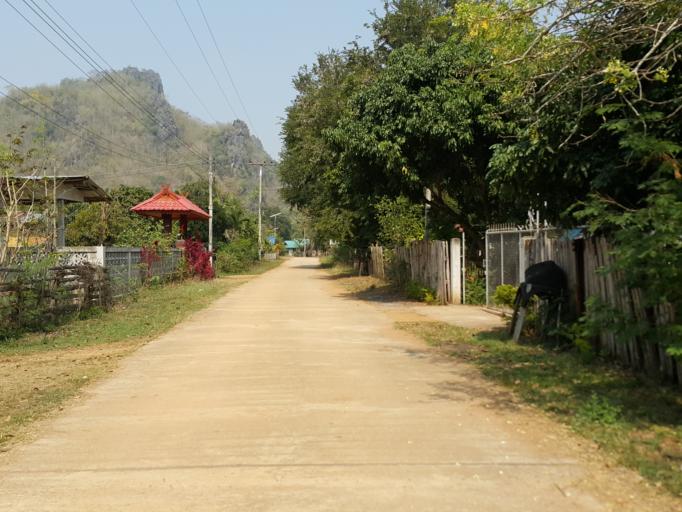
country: TH
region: Sukhothai
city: Thung Saliam
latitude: 17.3114
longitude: 99.5099
